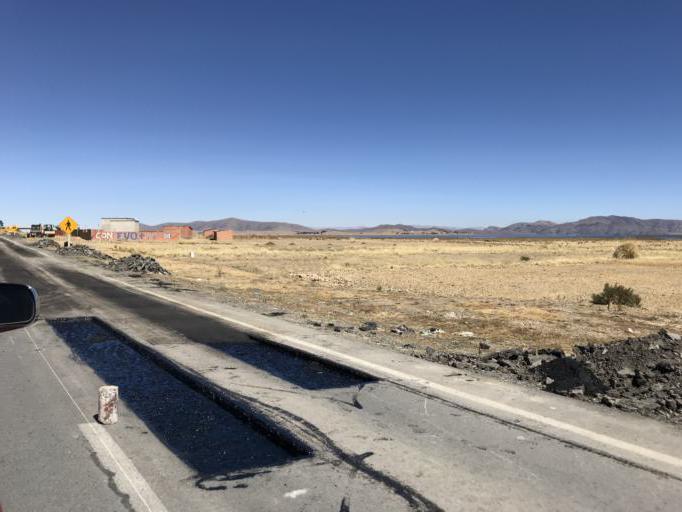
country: BO
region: La Paz
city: Huarina
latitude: -16.2328
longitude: -68.5785
